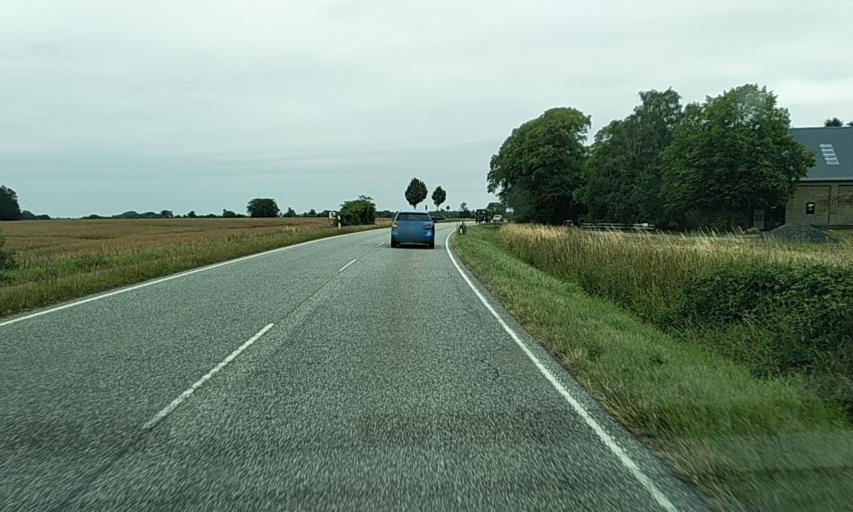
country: DE
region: Schleswig-Holstein
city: Grodersby
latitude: 54.6560
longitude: 9.8955
